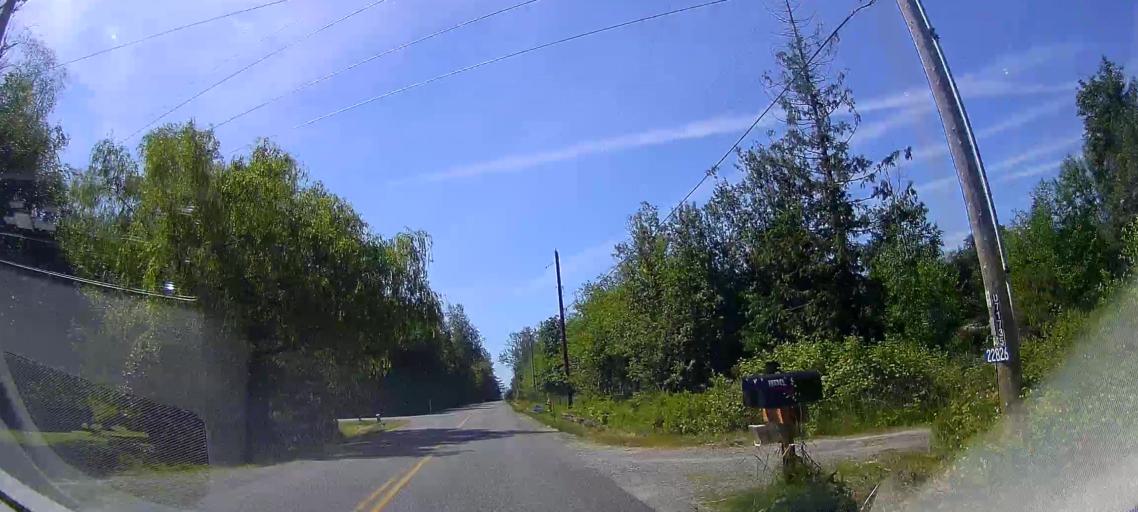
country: US
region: Washington
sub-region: Skagit County
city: Sedro-Woolley
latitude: 48.5360
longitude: -122.2482
